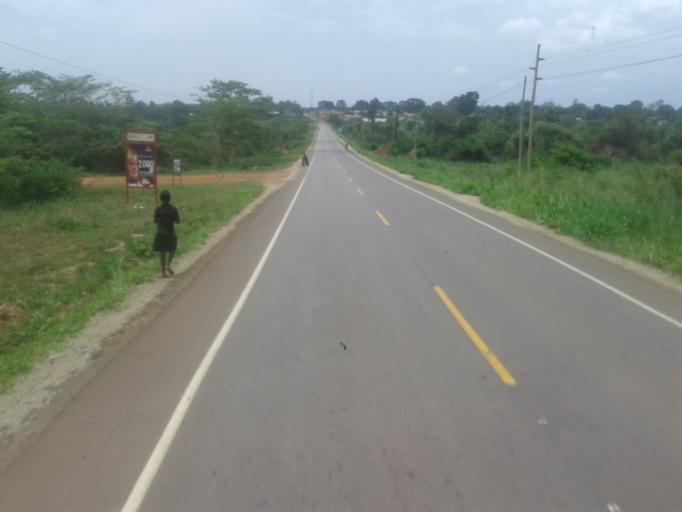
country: UG
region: Western Region
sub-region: Kiryandongo District
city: Kiryandongo
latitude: 1.8664
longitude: 32.0504
